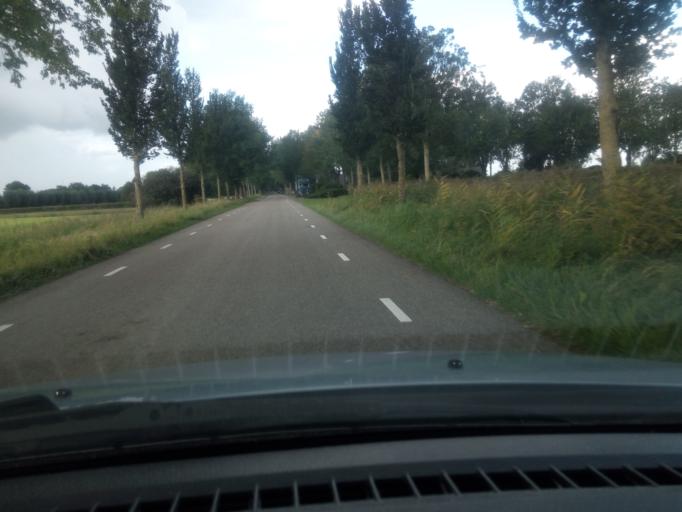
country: NL
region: Groningen
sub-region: Gemeente Zuidhorn
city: Grijpskerk
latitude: 53.2673
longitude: 6.2585
